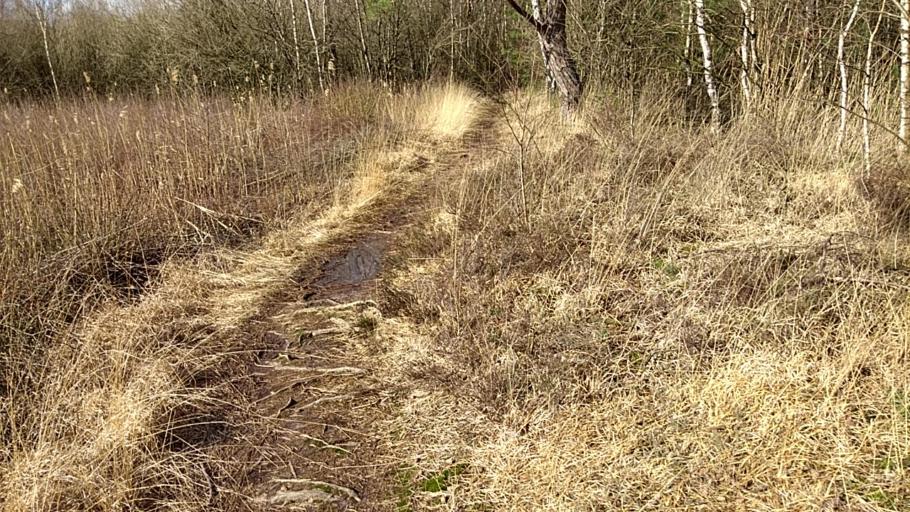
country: NL
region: Gelderland
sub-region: Gemeente Winterswijk
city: Winterswijk
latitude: 51.9915
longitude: 6.6604
